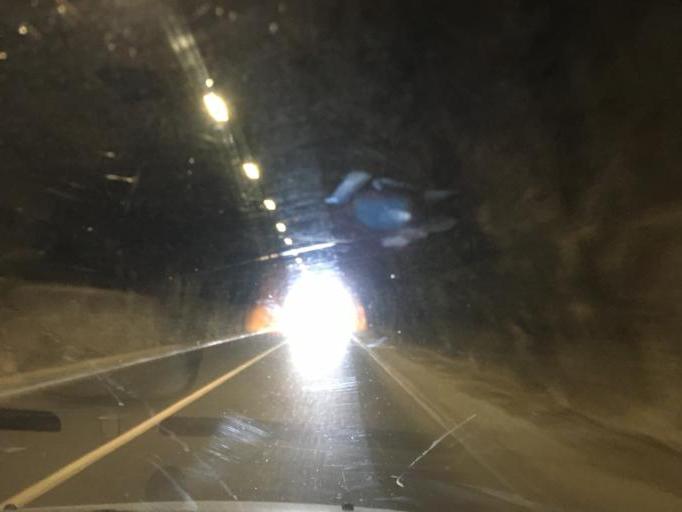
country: FR
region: Provence-Alpes-Cote d'Azur
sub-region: Departement des Alpes-Maritimes
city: Beaulieu-sur-Mer
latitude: 43.7164
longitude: 7.3327
